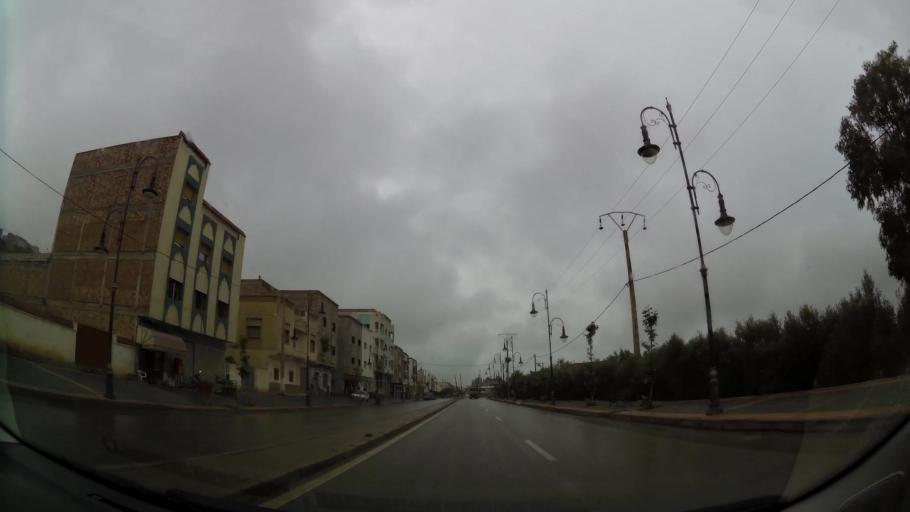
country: MA
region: Taza-Al Hoceima-Taounate
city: Imzourene
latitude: 35.1705
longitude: -3.8611
